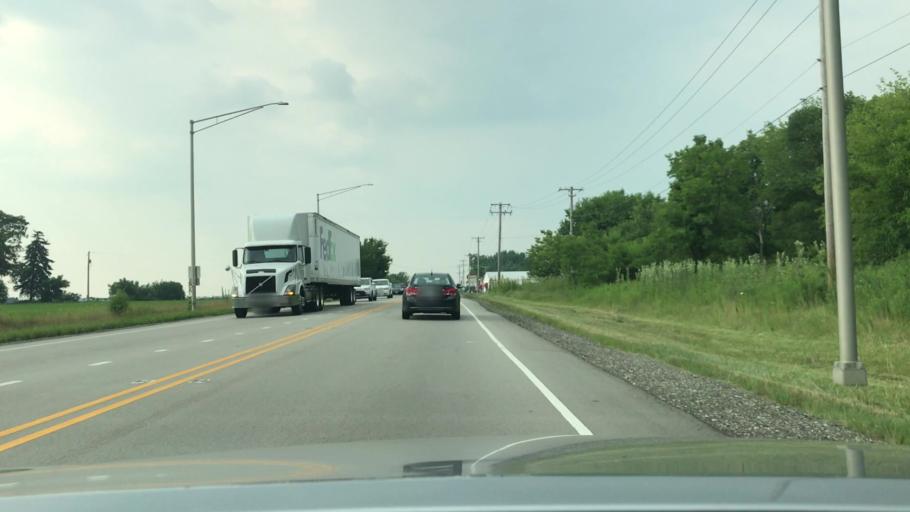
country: US
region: Illinois
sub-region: Will County
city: Plainfield
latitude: 41.6525
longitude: -88.2312
